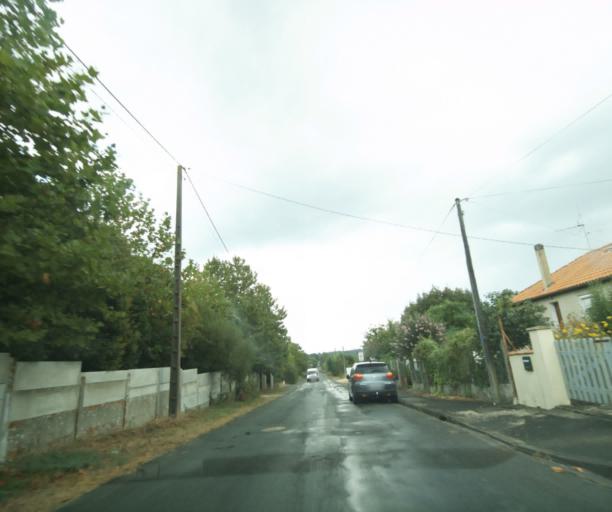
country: FR
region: Poitou-Charentes
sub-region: Departement de la Charente-Maritime
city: Tonnay-Charente
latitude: 45.9435
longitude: -0.8812
